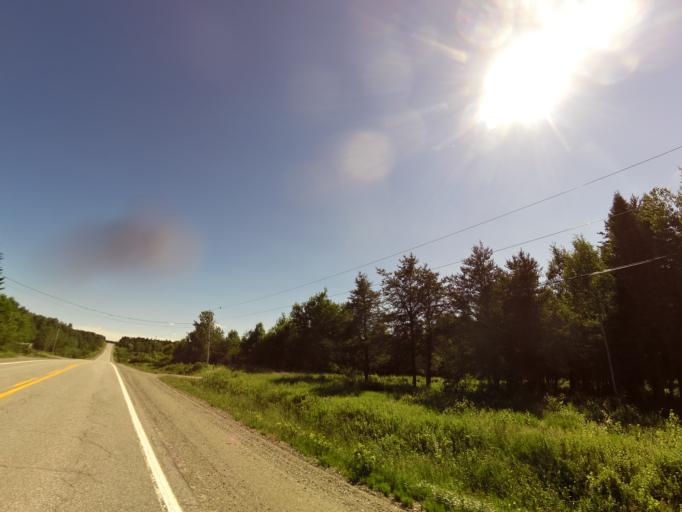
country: CA
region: Quebec
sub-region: Abitibi-Temiscamingue
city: Senneterre
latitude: 48.1593
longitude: -77.3652
